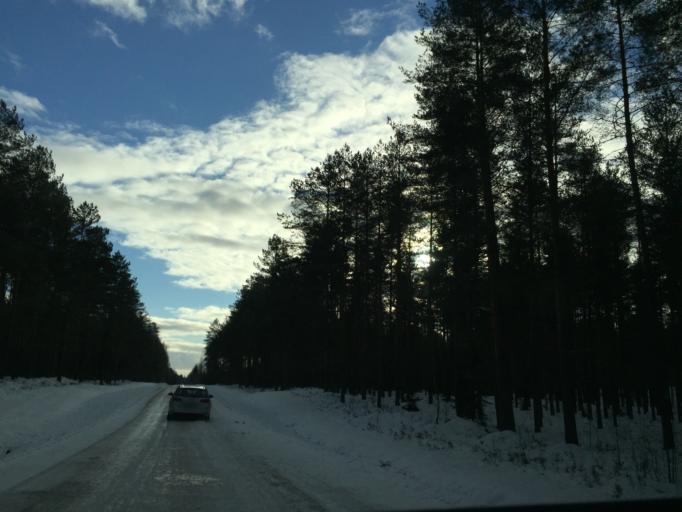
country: LV
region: Ogre
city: Jumprava
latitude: 56.5601
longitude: 24.8548
